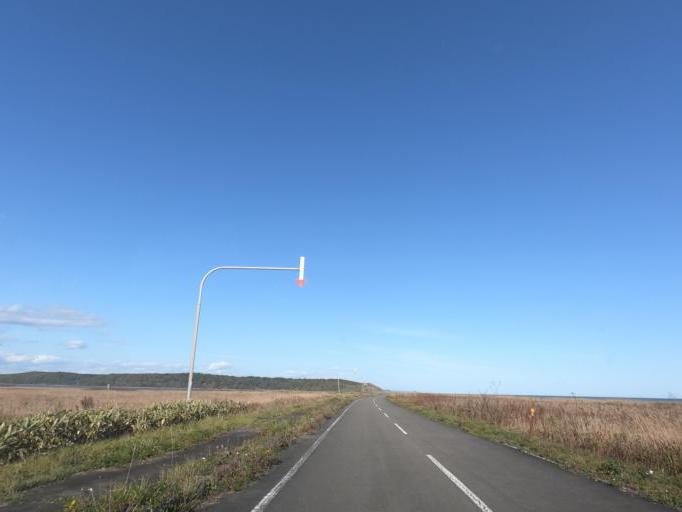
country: JP
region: Hokkaido
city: Obihiro
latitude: 42.5919
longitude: 143.5417
